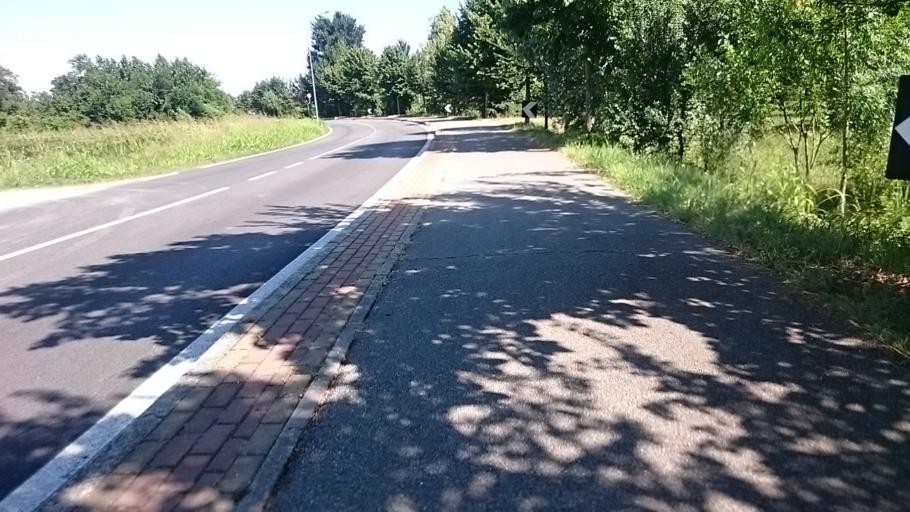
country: IT
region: Veneto
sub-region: Provincia di Venezia
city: Arino
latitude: 45.4276
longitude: 12.0581
